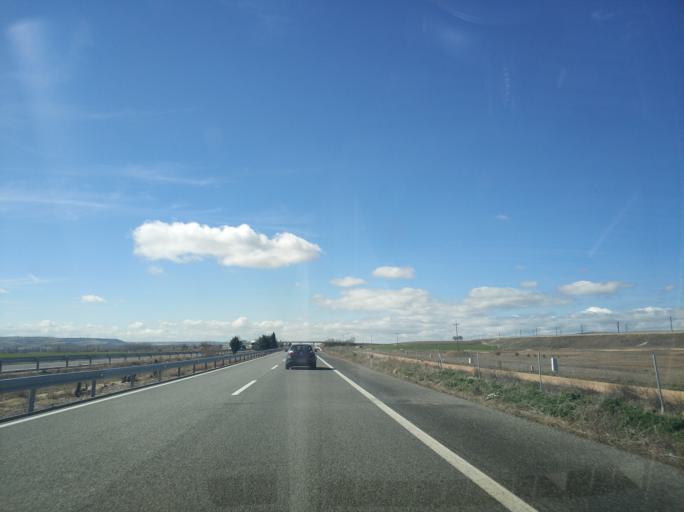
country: ES
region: Castille and Leon
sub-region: Provincia de Burgos
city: Villazopeque
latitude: 42.1932
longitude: -4.0304
